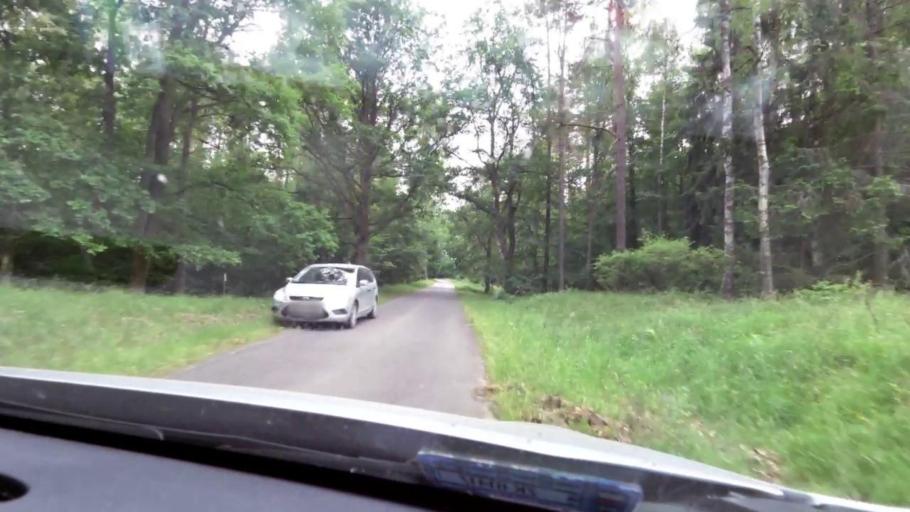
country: PL
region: Pomeranian Voivodeship
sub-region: Powiat bytowski
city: Trzebielino
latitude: 54.2421
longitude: 16.9998
